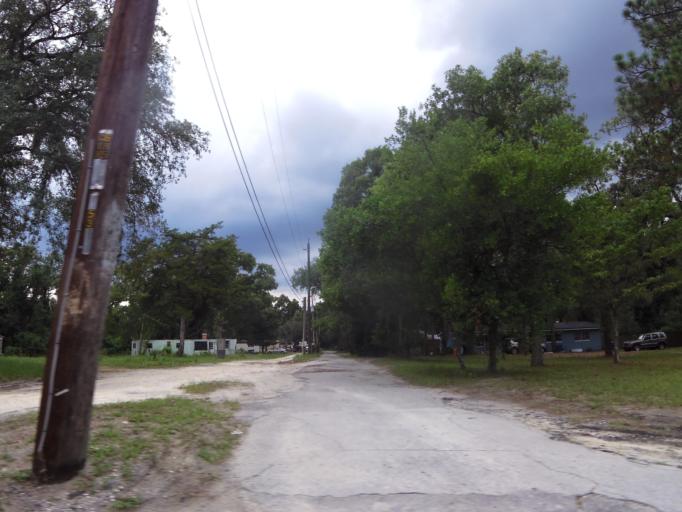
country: US
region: Florida
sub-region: Duval County
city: Jacksonville
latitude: 30.3340
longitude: -81.5373
